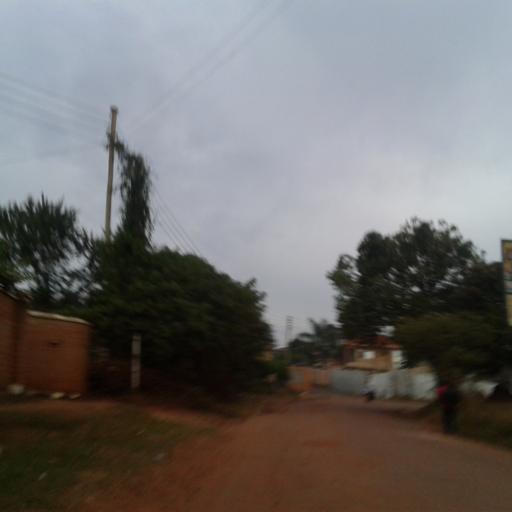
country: UG
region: Central Region
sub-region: Kampala District
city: Kampala
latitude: 0.2480
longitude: 32.6191
